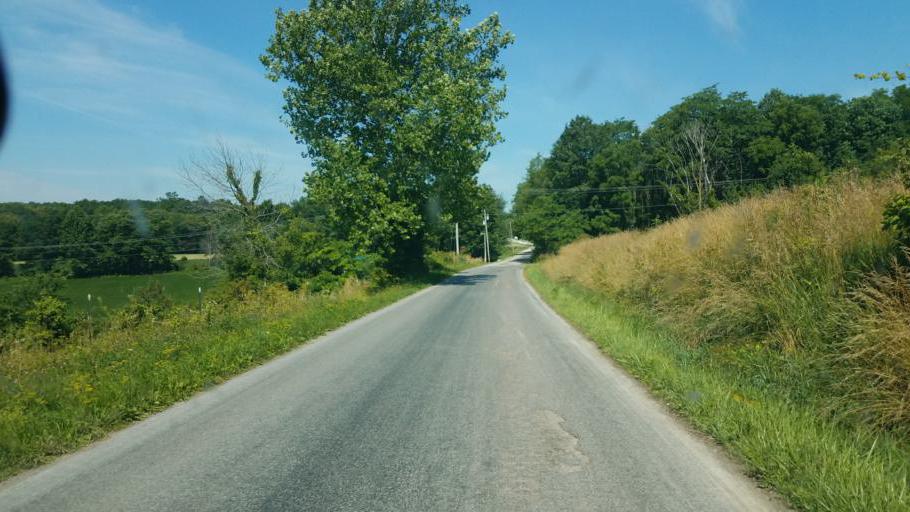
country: US
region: Ohio
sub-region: Knox County
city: Fredericktown
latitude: 40.5506
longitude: -82.6227
